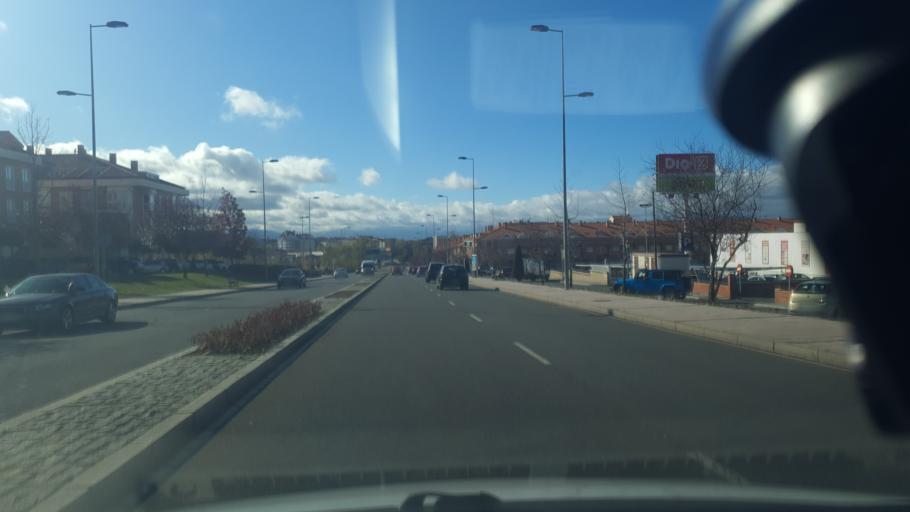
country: ES
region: Castille and Leon
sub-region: Provincia de Avila
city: Avila
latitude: 40.6616
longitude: -4.6748
